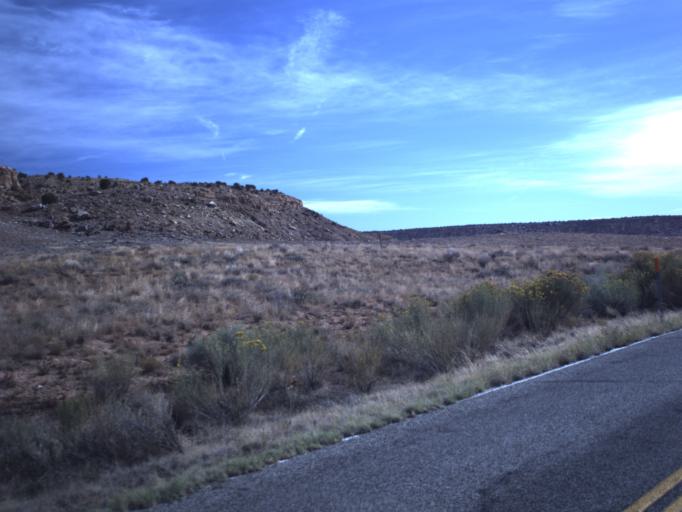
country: US
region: Utah
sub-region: San Juan County
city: Blanding
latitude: 37.4229
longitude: -109.4709
